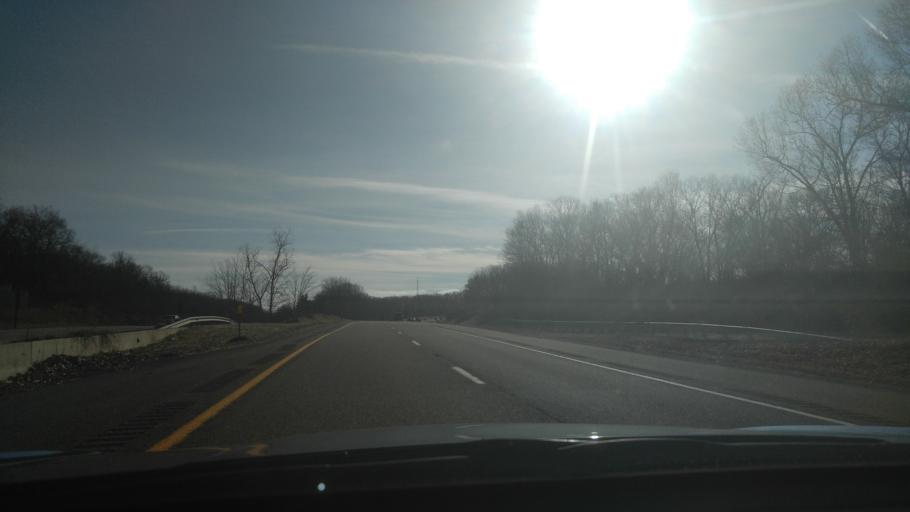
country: US
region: Rhode Island
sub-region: Providence County
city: Cumberland Hill
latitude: 41.9578
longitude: -71.4830
